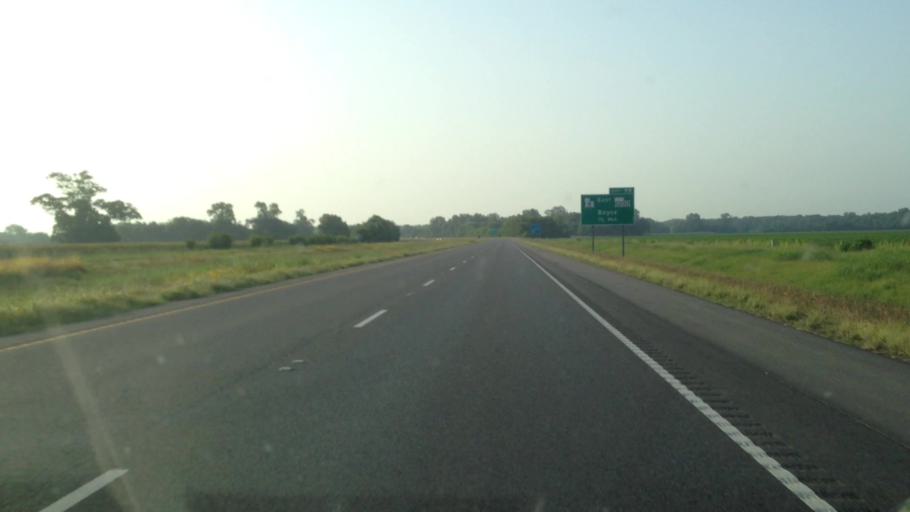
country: US
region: Louisiana
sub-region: Rapides Parish
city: Boyce
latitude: 31.3855
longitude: -92.6832
